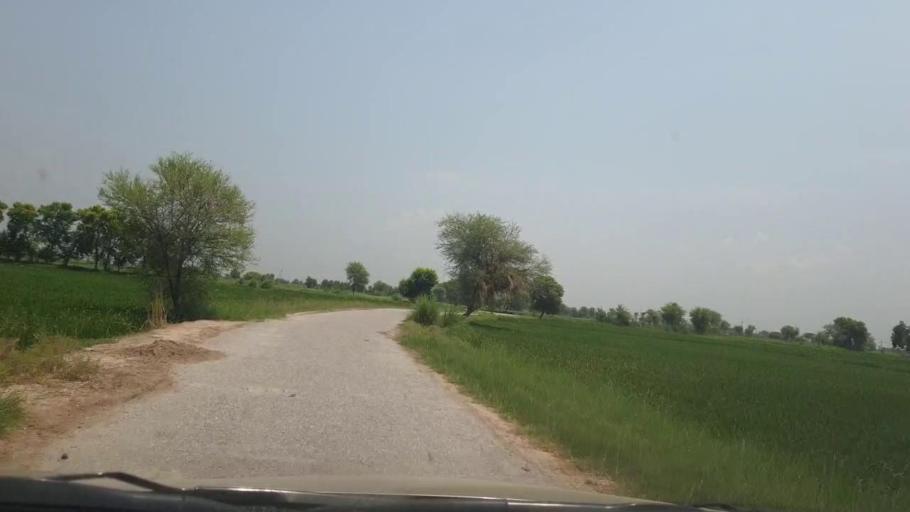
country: PK
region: Sindh
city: Ratodero
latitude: 27.7353
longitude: 68.3014
